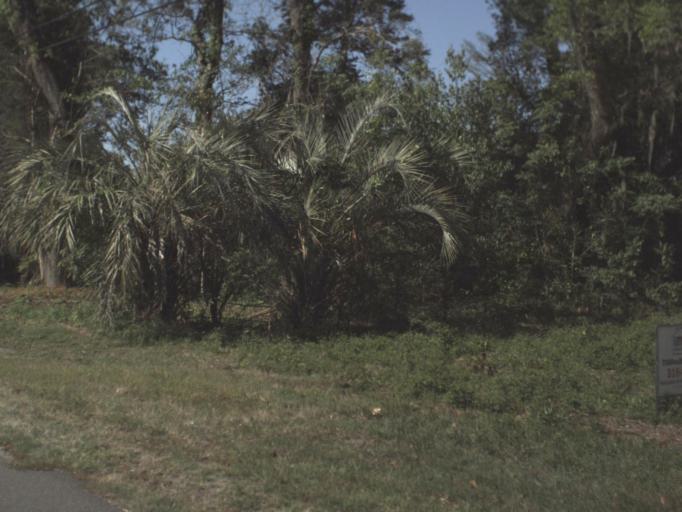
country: US
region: Florida
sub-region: Escambia County
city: Ferry Pass
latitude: 30.5313
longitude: -87.1893
